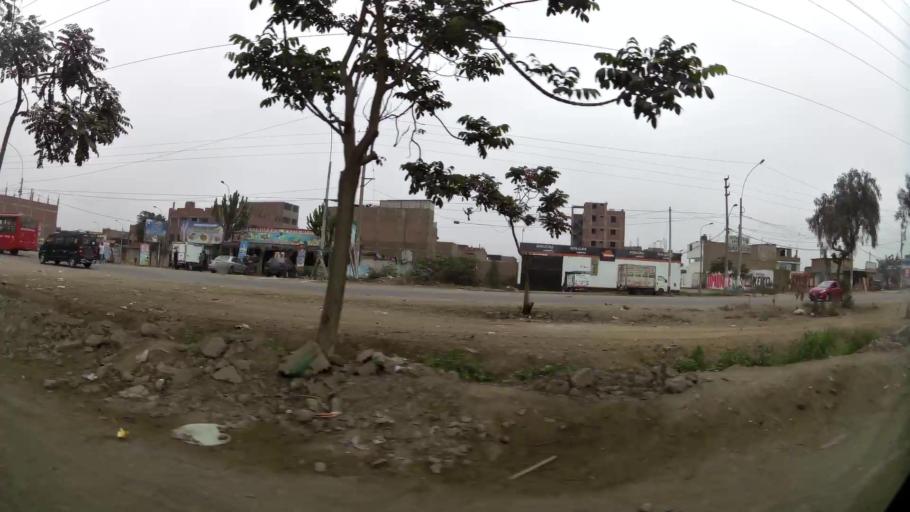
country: PE
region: Lima
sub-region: Lima
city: Urb. Santo Domingo
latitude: -11.9021
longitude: -77.0513
